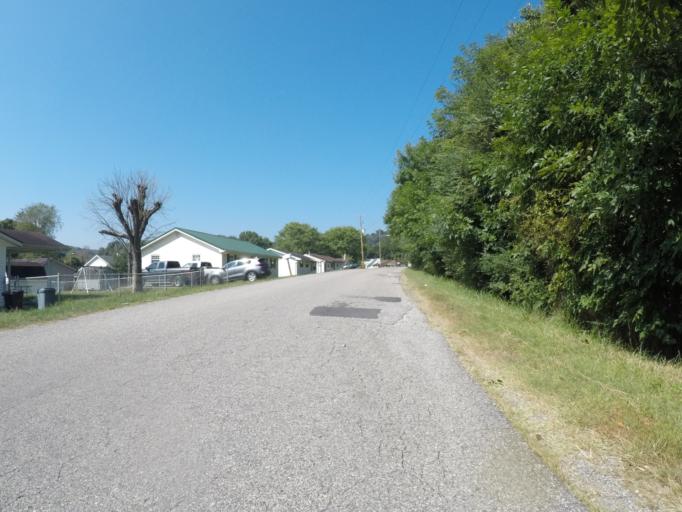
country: US
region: West Virginia
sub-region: Cabell County
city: Barboursville
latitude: 38.3707
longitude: -82.2728
